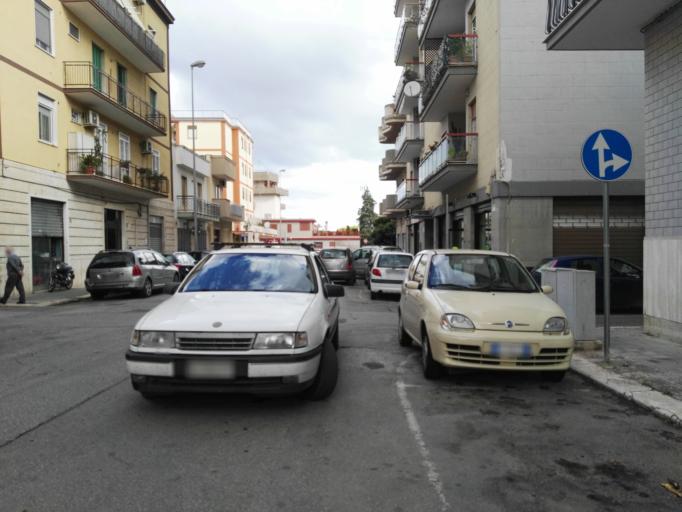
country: IT
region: Apulia
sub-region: Provincia di Bari
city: Triggiano
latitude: 41.0621
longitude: 16.9168
